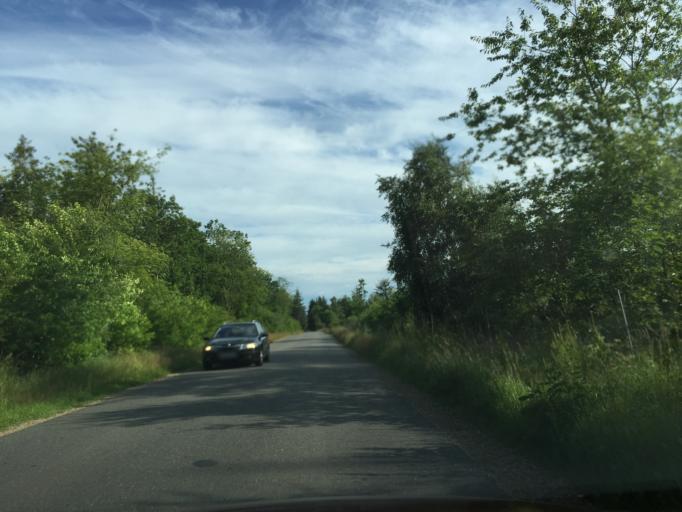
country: DK
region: Central Jutland
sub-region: Silkeborg Kommune
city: Svejbaek
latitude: 56.2303
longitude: 9.6814
